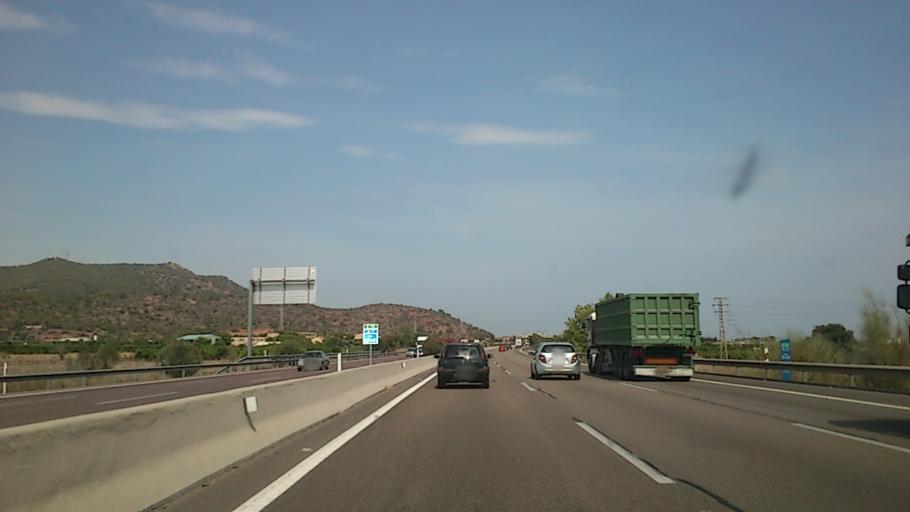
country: ES
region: Valencia
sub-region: Provincia de Valencia
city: Pucol
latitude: 39.6180
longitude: -0.3354
